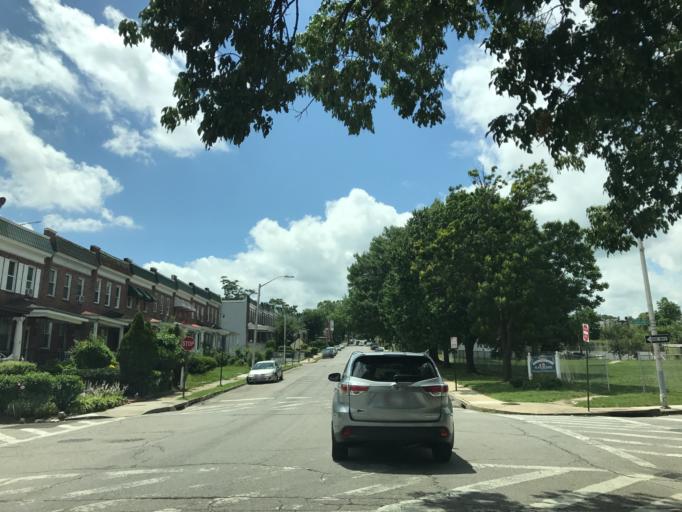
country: US
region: Maryland
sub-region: City of Baltimore
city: Baltimore
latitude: 39.3061
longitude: -76.6629
